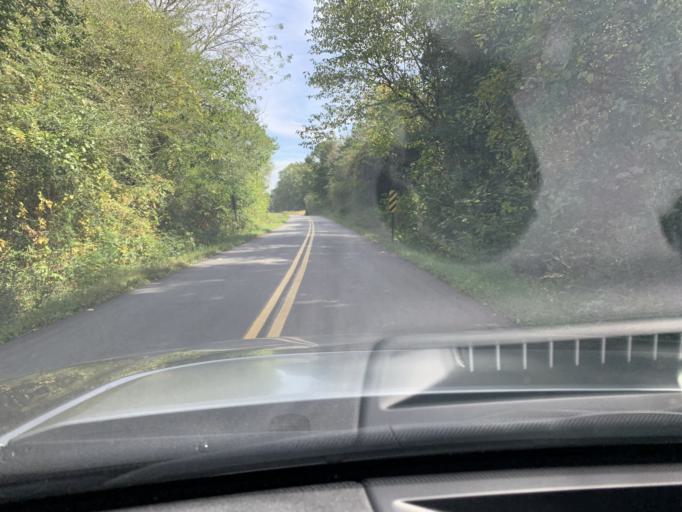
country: US
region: Georgia
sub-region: Polk County
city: Cedartown
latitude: 33.9478
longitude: -85.3627
